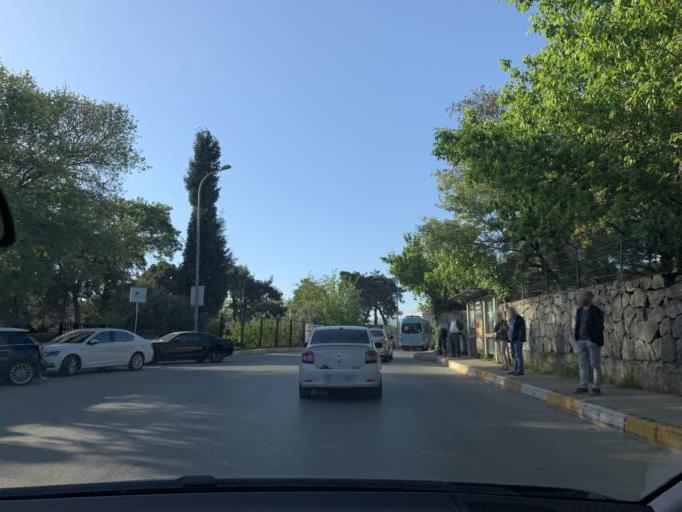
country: TR
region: Istanbul
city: Icmeler
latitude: 40.8443
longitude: 29.2956
